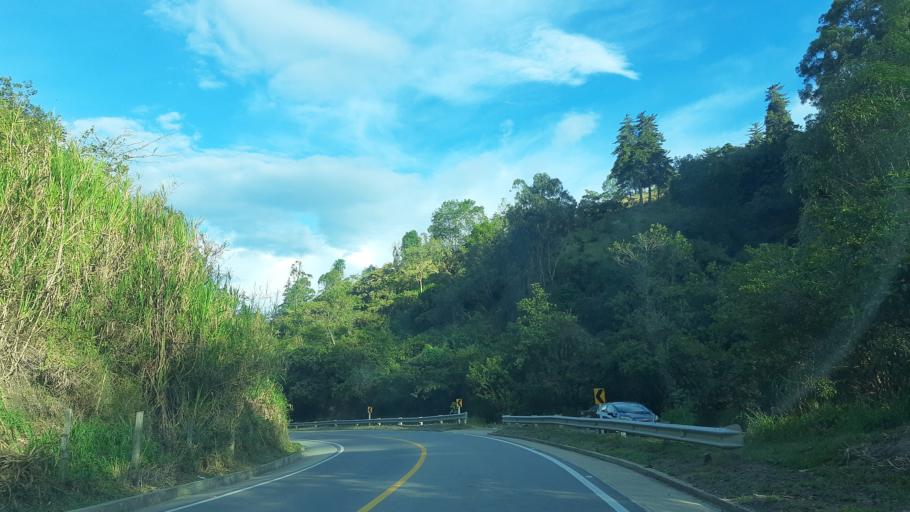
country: CO
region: Cundinamarca
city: Macheta
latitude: 5.0755
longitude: -73.5654
